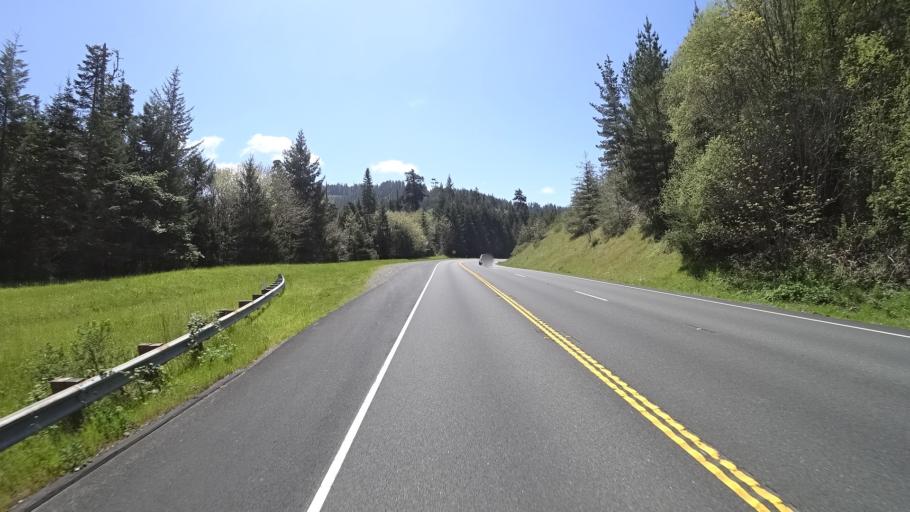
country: US
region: California
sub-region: Humboldt County
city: Blue Lake
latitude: 40.9023
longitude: -123.9173
